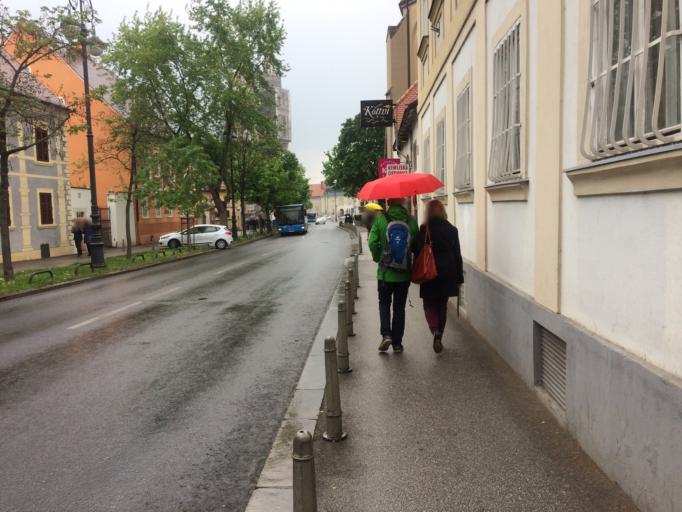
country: HR
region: Grad Zagreb
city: Zagreb
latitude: 45.8171
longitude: 15.9781
